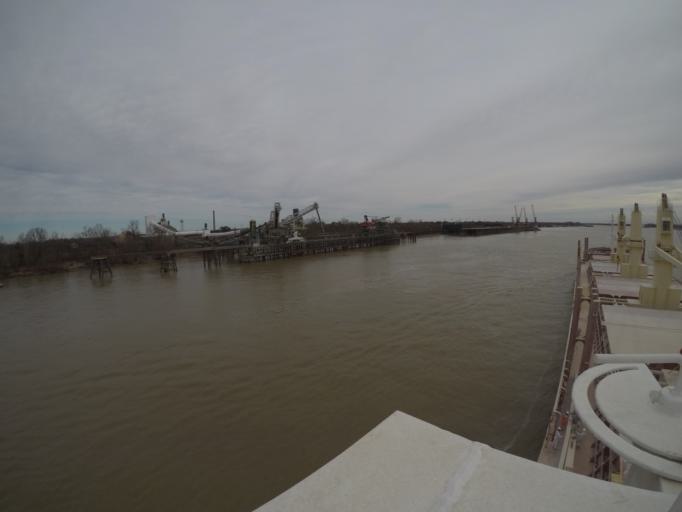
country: US
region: Louisiana
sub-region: Saint John the Baptist Parish
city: Edgard
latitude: 30.0529
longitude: -90.5710
